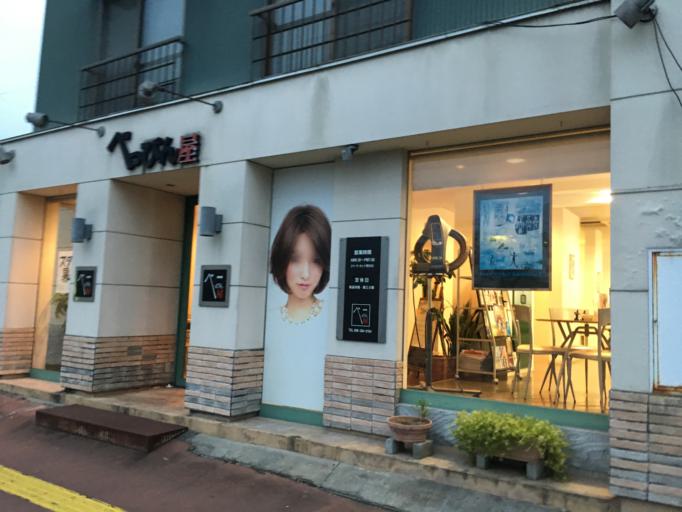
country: JP
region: Kumamoto
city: Kumamoto
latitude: 32.7968
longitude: 130.7272
